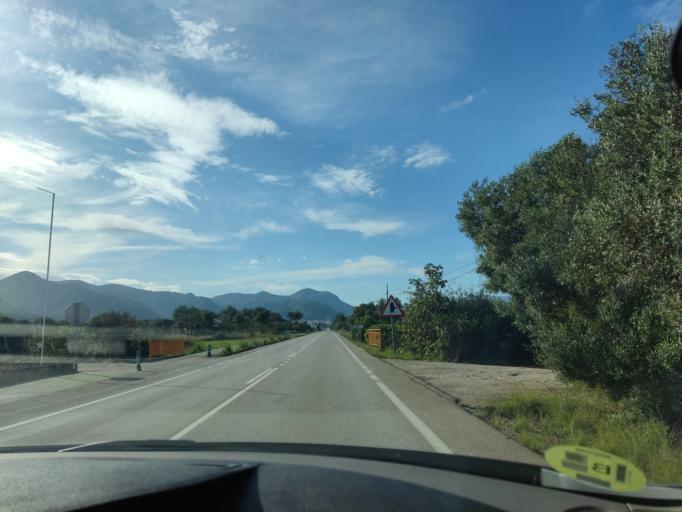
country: ES
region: Valencia
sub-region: Provincia de Alicante
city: Pego
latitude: 38.8469
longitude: -0.0873
